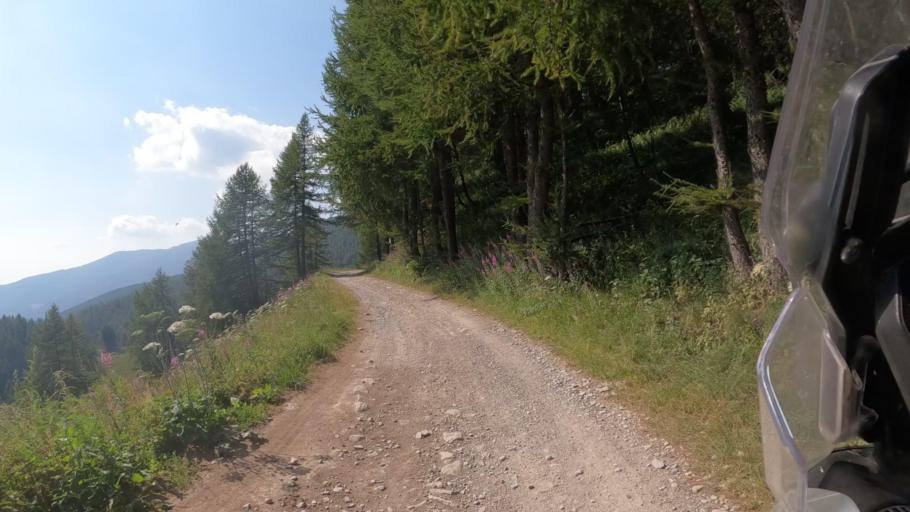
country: IT
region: Piedmont
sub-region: Provincia di Cuneo
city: Briga Alta
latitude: 44.0941
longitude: 7.7217
